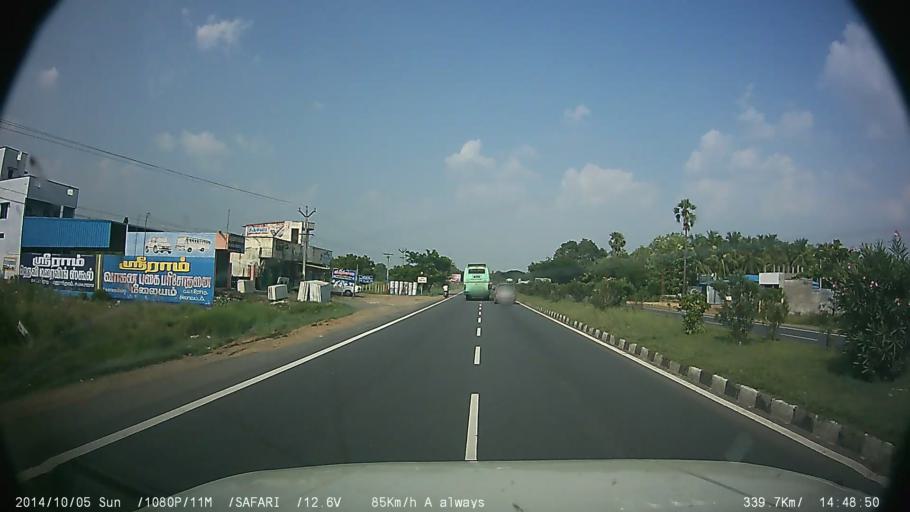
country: IN
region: Tamil Nadu
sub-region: Kancheepuram
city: Madurantakam
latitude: 12.4919
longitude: 79.8684
